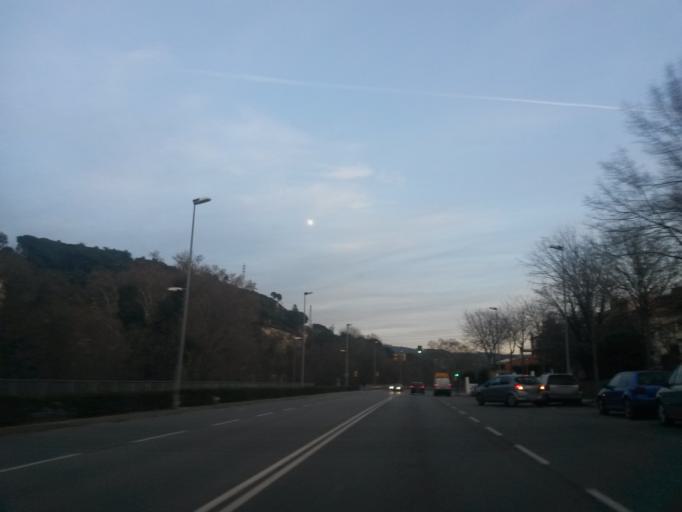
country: ES
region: Catalonia
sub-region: Provincia de Girona
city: Girona
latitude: 41.9734
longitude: 2.8295
